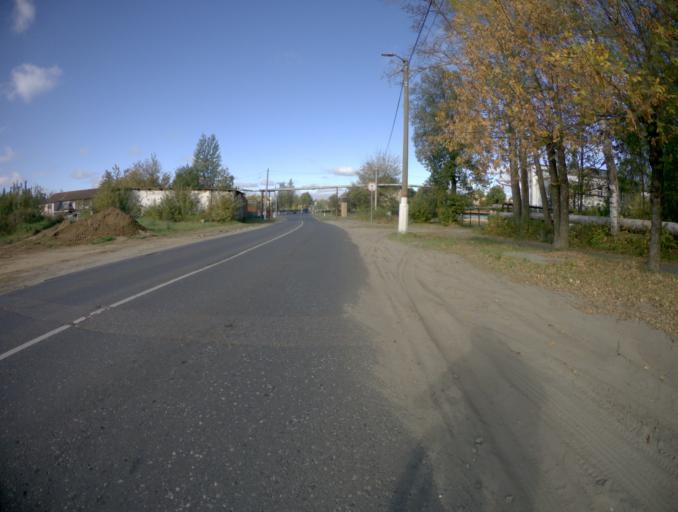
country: RU
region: Moskovskaya
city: Roshal'
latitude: 55.6622
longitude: 39.8710
